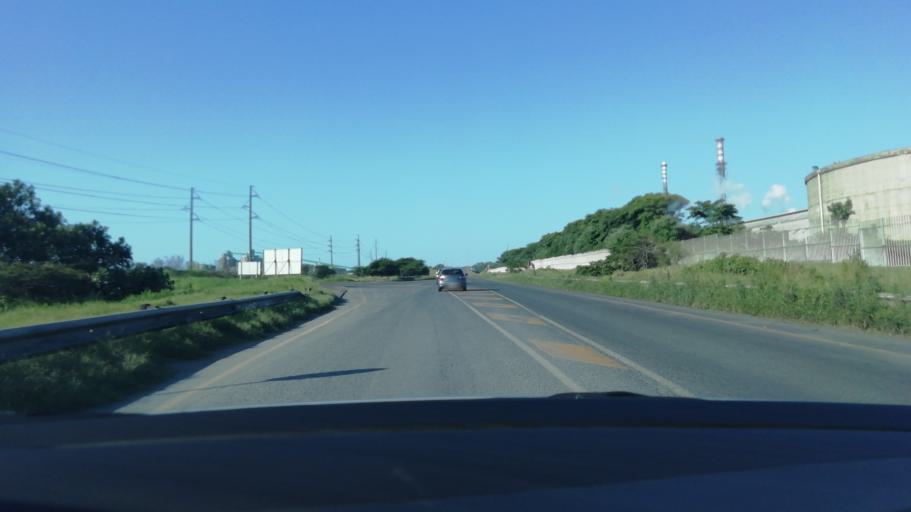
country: ZA
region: KwaZulu-Natal
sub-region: uThungulu District Municipality
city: Richards Bay
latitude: -28.7757
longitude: 32.0314
